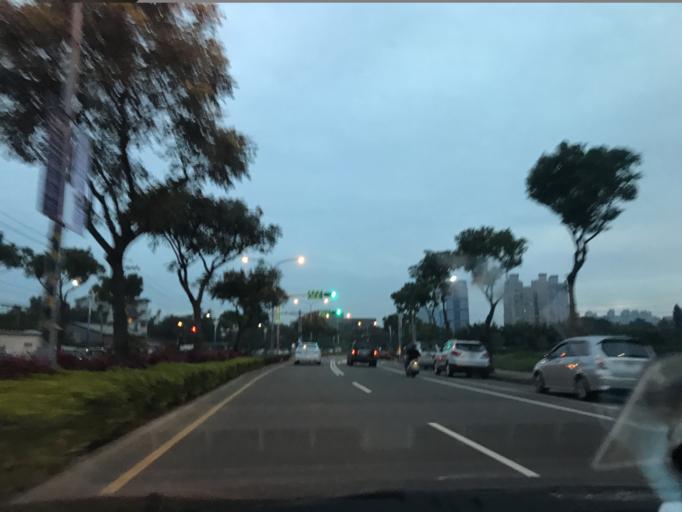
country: TW
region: Taiwan
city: Daxi
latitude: 24.9372
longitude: 121.2402
